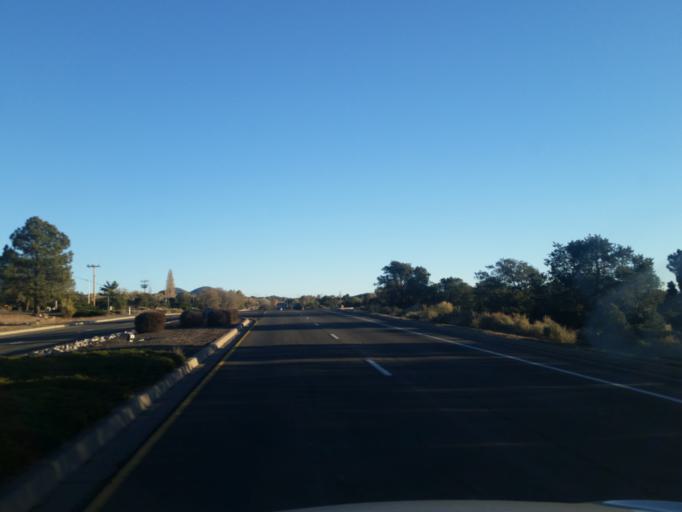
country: US
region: New Mexico
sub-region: Santa Fe County
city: Santa Fe
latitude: 35.6486
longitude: -105.9347
